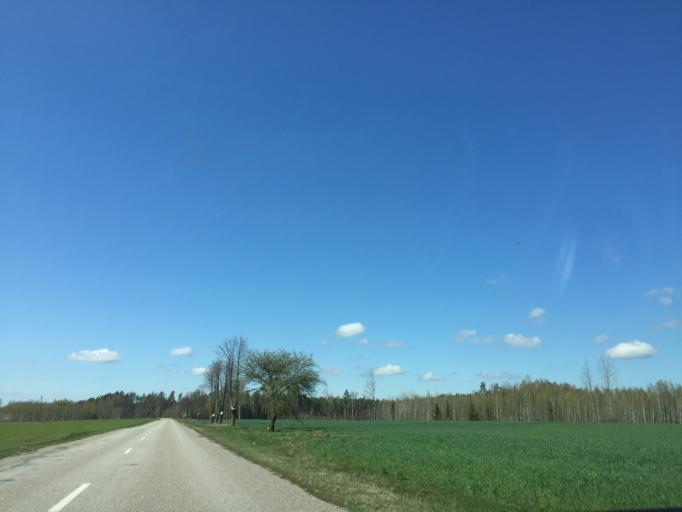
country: LV
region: Strenci
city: Seda
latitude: 57.5691
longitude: 25.8074
